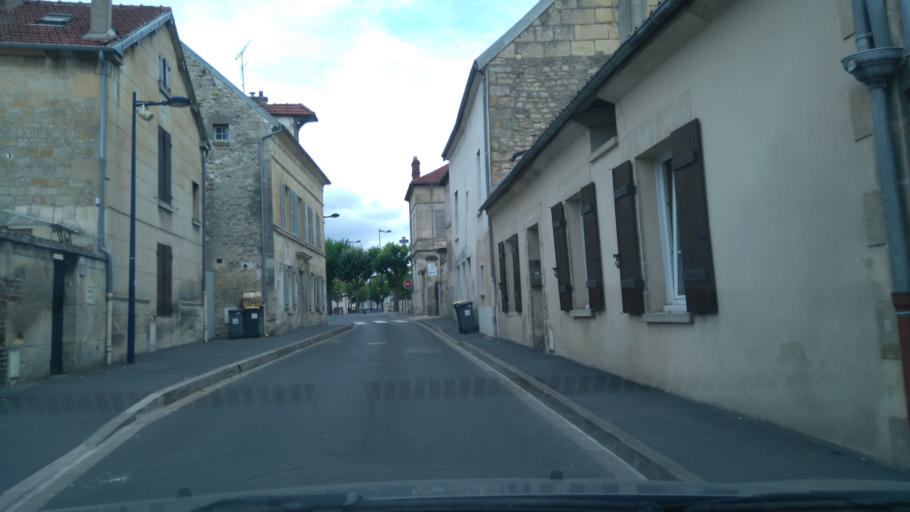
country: FR
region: Picardie
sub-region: Departement de l'Oise
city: Gouvieux
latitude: 49.1891
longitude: 2.4149
